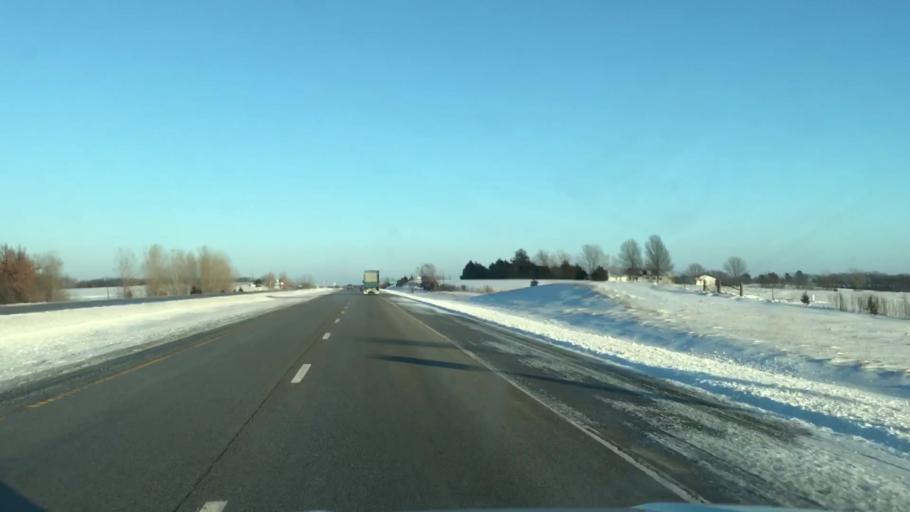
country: US
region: Missouri
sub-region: Clinton County
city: Gower
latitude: 39.7470
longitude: -94.6177
